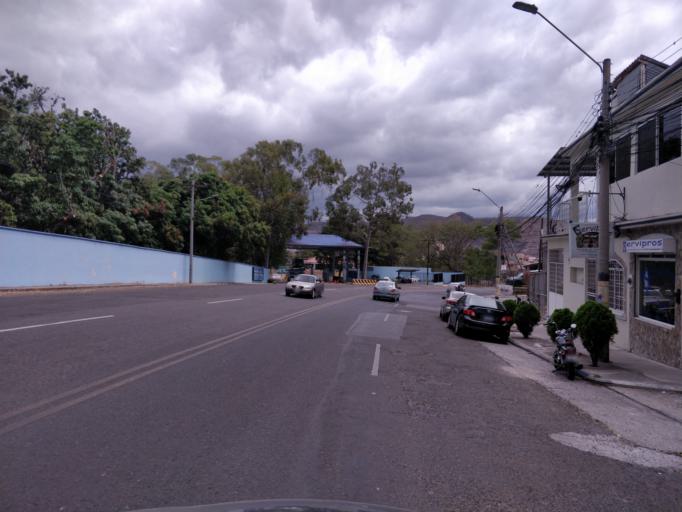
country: HN
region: Francisco Morazan
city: Tegucigalpa
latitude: 14.0518
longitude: -87.2175
